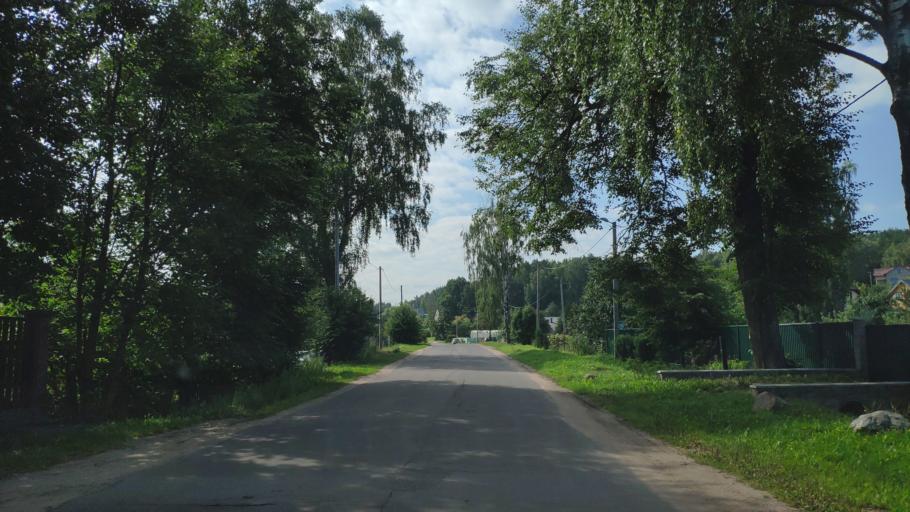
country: BY
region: Minsk
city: Zaslawye
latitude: 53.9916
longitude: 27.2848
